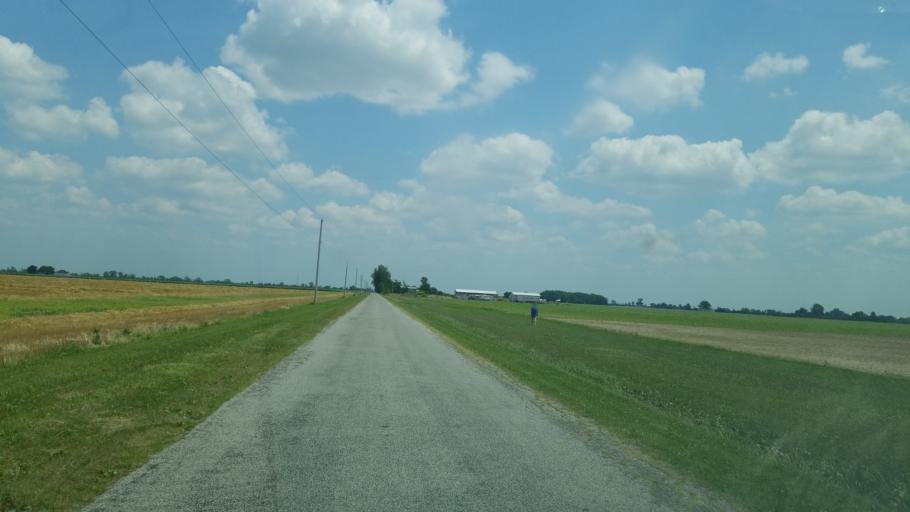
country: US
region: Ohio
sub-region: Henry County
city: Deshler
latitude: 41.2552
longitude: -83.8582
